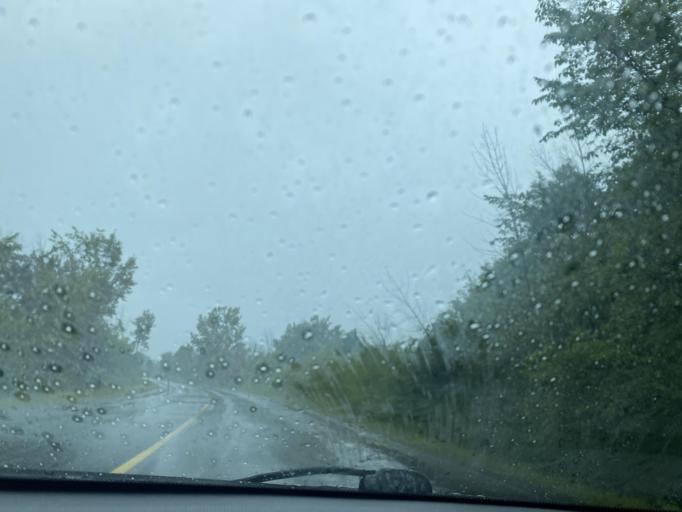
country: CA
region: Quebec
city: Baie-D'Urfe
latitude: 45.4432
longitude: -73.9134
